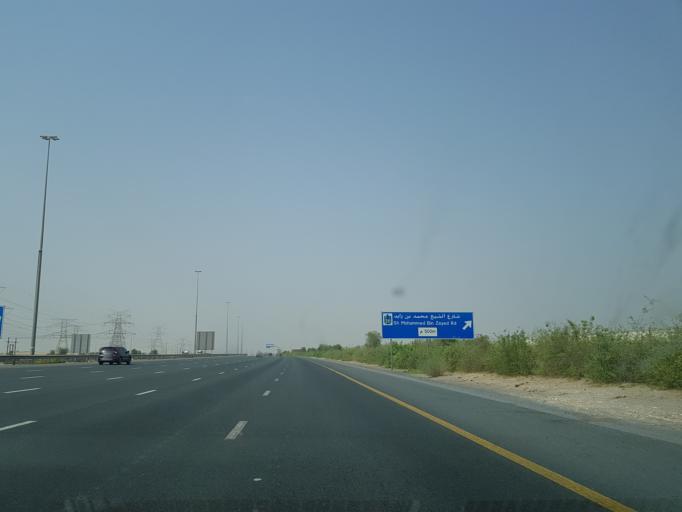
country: AE
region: Dubai
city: Dubai
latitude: 25.0560
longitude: 55.3160
